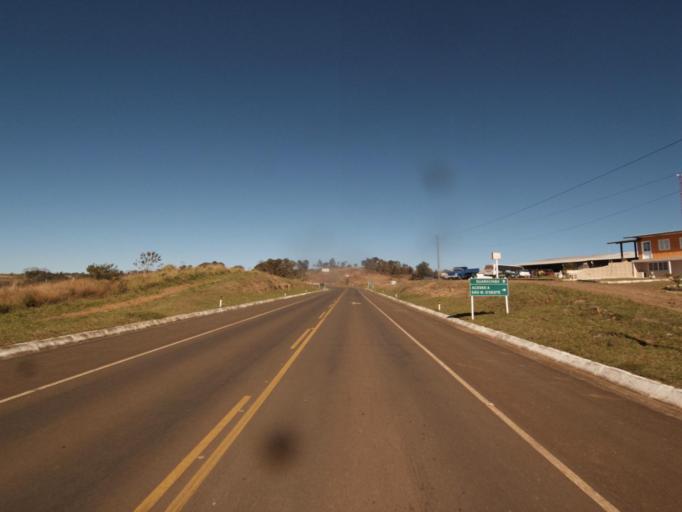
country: AR
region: Misiones
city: Bernardo de Irigoyen
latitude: -26.7028
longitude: -53.5274
